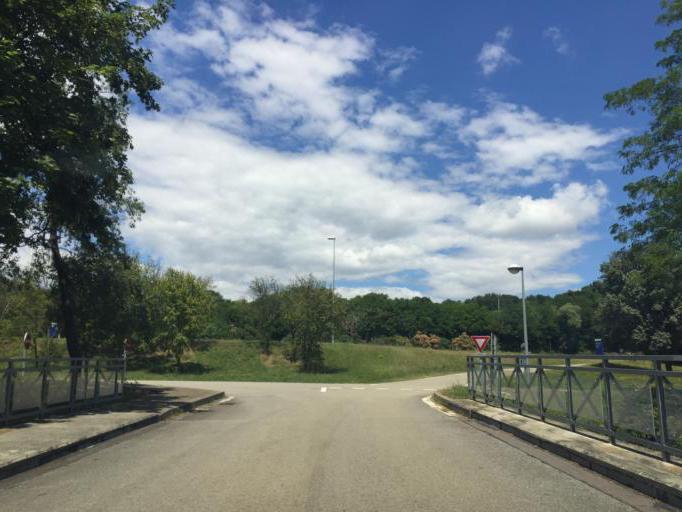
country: FR
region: Rhone-Alpes
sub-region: Departement de la Drome
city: Mercurol
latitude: 45.0786
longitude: 4.8727
